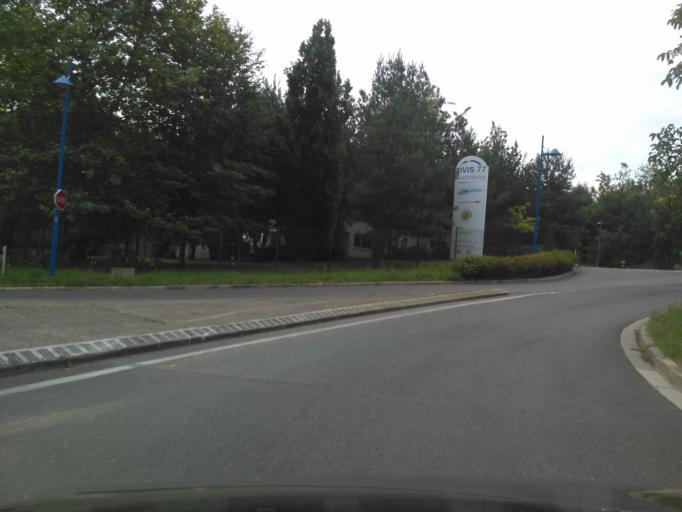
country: FR
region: Ile-de-France
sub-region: Departement de Seine-et-Marne
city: Vaux-le-Penil
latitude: 48.5418
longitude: 2.6884
